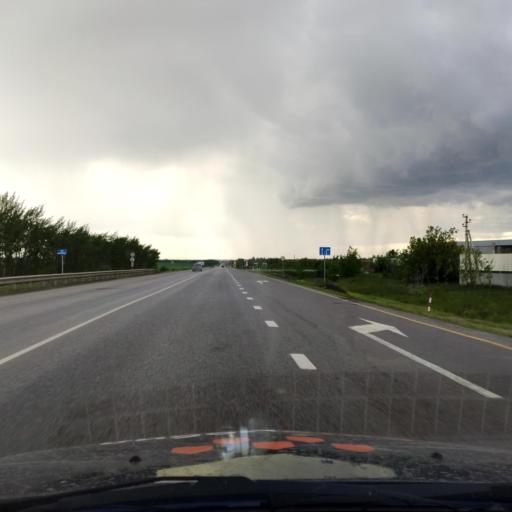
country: RU
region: Voronezj
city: Novaya Usman'
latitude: 51.6852
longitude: 39.4789
